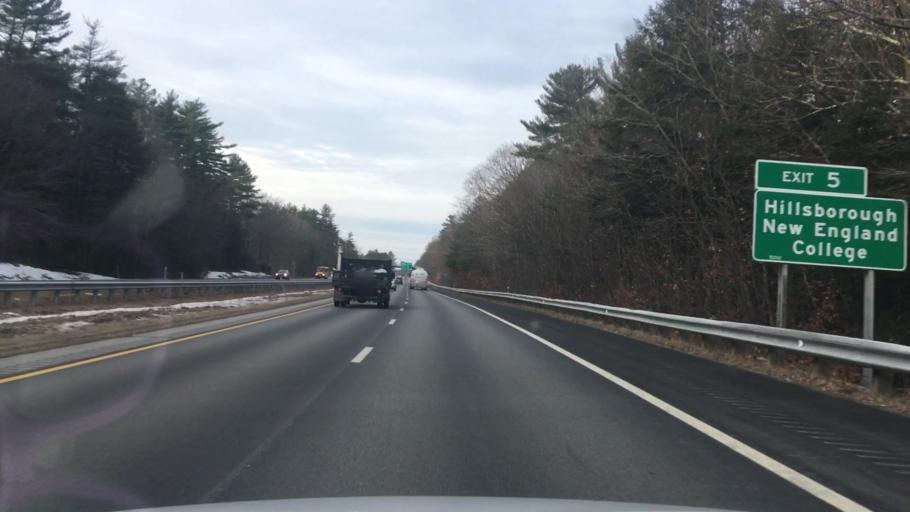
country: US
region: New Hampshire
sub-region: Merrimack County
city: Hopkinton
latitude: 43.1838
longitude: -71.6679
